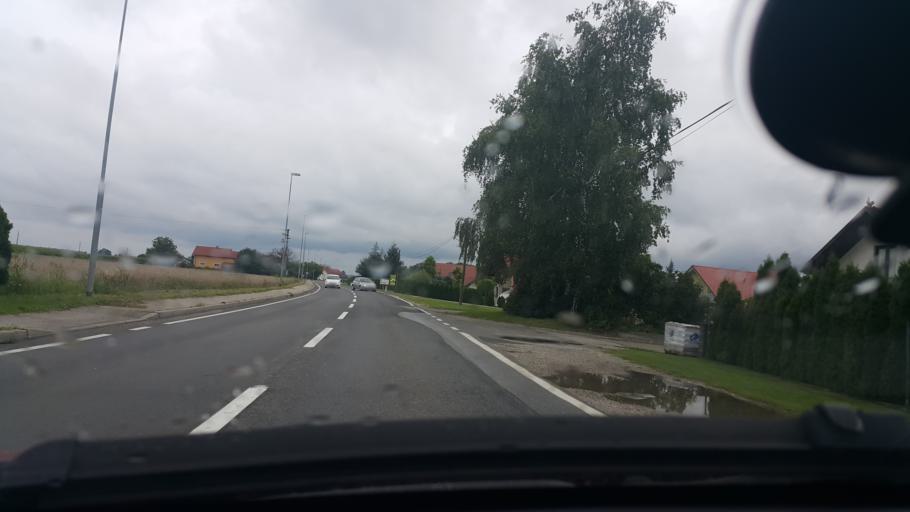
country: SI
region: Gorisnica
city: Gorisnica
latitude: 46.4140
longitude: 16.0084
